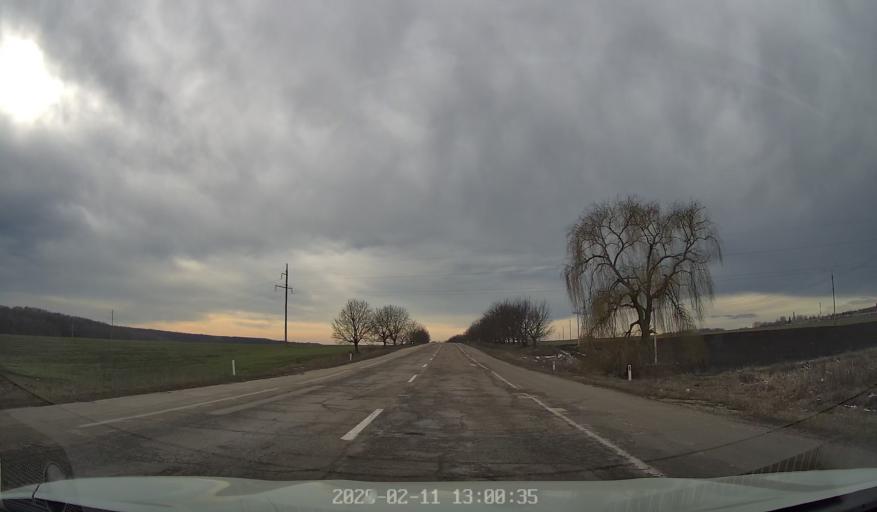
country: MD
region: Briceni
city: Briceni
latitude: 48.3246
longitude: 27.0169
